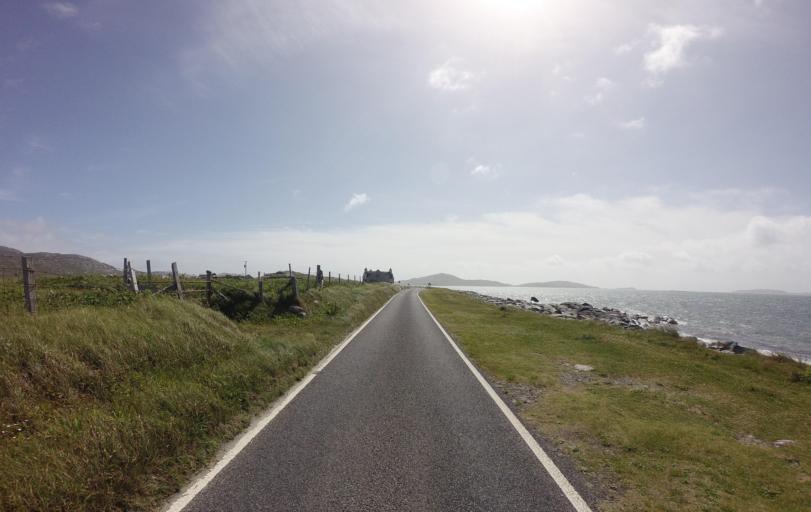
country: GB
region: Scotland
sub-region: Eilean Siar
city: Isle of South Uist
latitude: 57.1033
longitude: -7.3602
